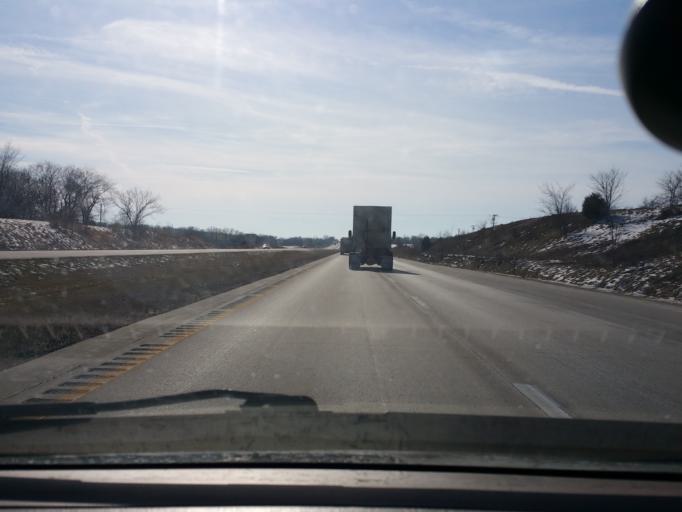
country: US
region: Missouri
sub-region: Clinton County
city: Cameron
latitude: 39.6640
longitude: -94.2368
